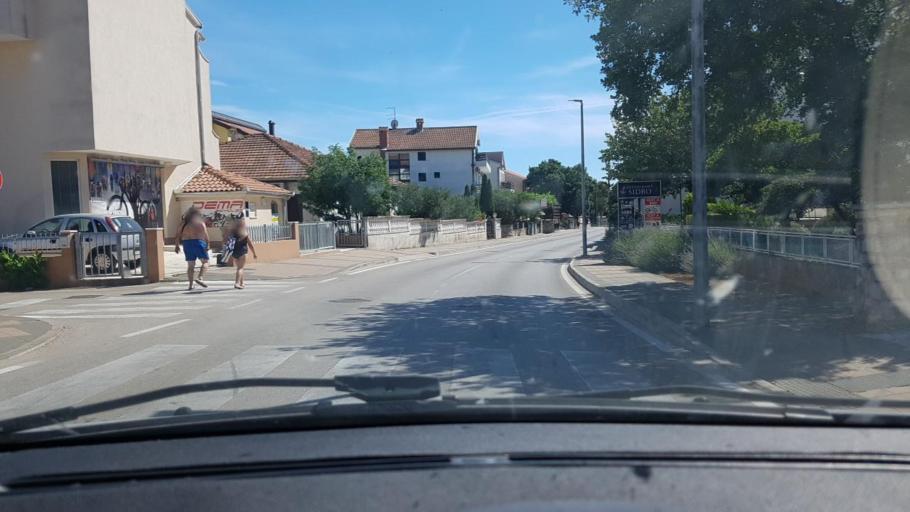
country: HR
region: Sibensko-Kniniska
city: Vodice
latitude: 43.7563
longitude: 15.7894
